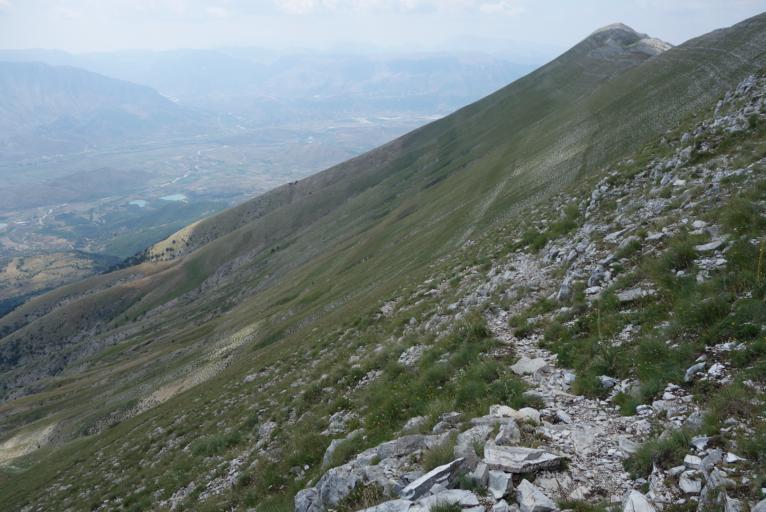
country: AL
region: Gjirokaster
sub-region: Rrethi i Gjirokastres
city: Saraqinishte
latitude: 40.1355
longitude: 20.2448
